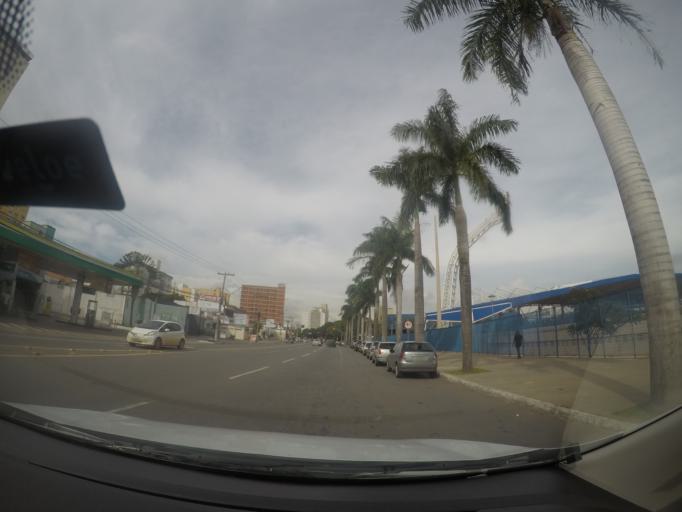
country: BR
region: Goias
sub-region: Goiania
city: Goiania
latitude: -16.6716
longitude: -49.2616
